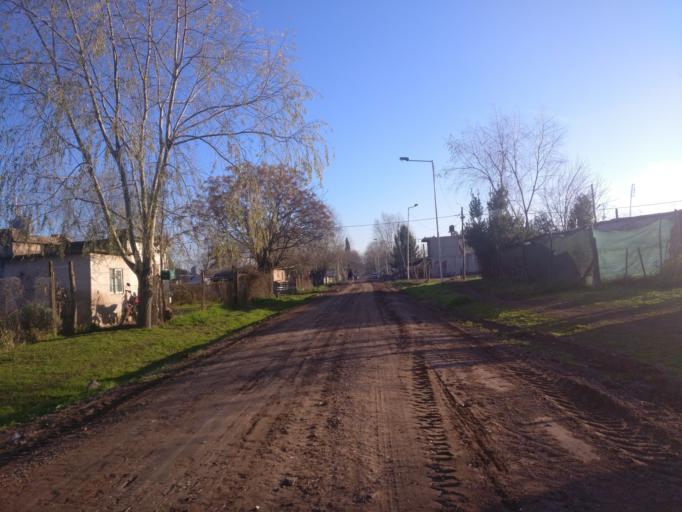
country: AR
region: Buenos Aires
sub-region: Partido de Ezeiza
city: Ezeiza
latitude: -34.9408
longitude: -58.6045
